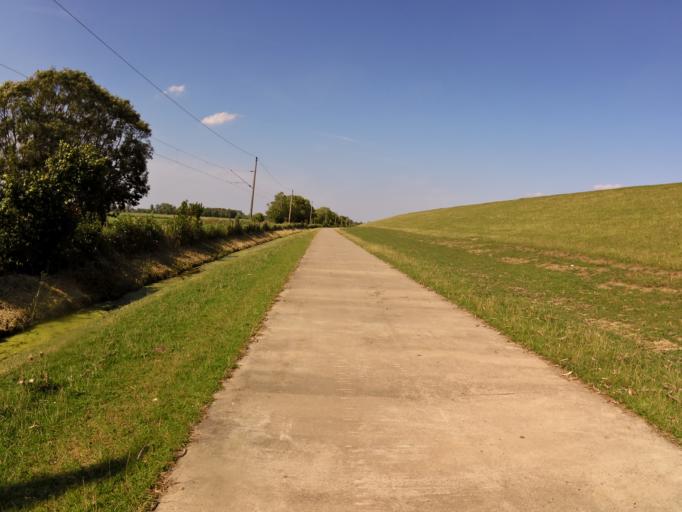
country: DE
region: Lower Saxony
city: Nordenham
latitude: 53.4540
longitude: 8.4749
